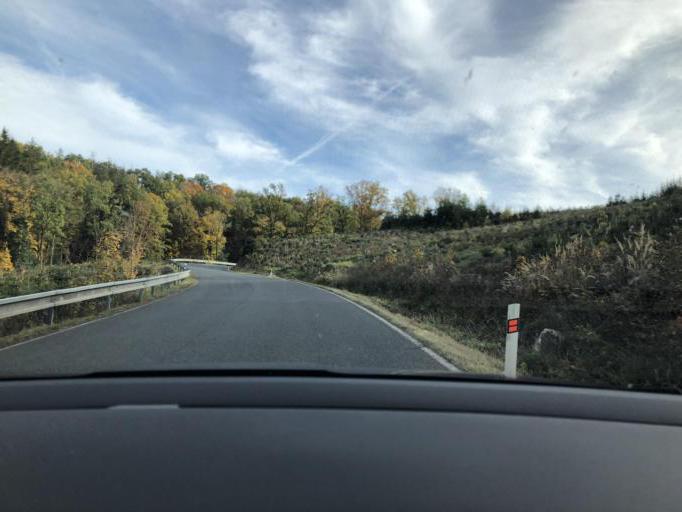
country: CZ
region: Central Bohemia
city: Divisov
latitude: 49.8041
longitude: 14.9259
